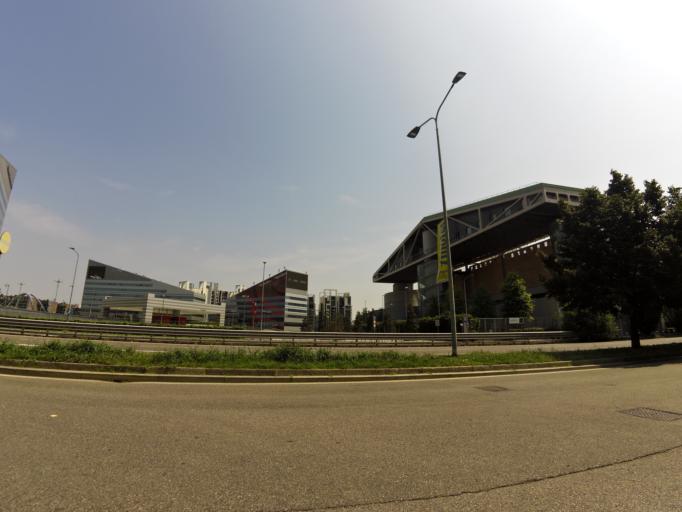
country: IT
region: Lombardy
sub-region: Citta metropolitana di Milano
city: Novate Milanese
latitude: 45.4841
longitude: 9.1463
